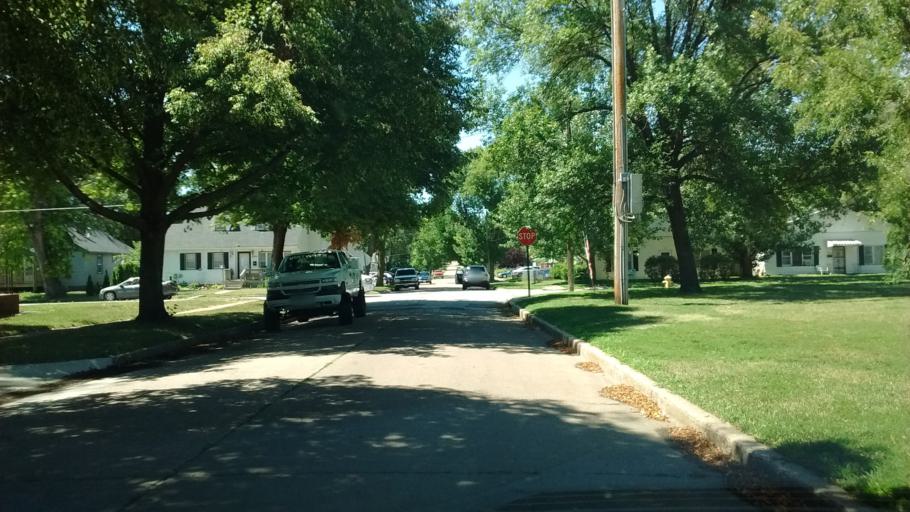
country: US
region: Iowa
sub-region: Woodbury County
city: Sioux City
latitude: 42.5208
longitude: -96.4252
